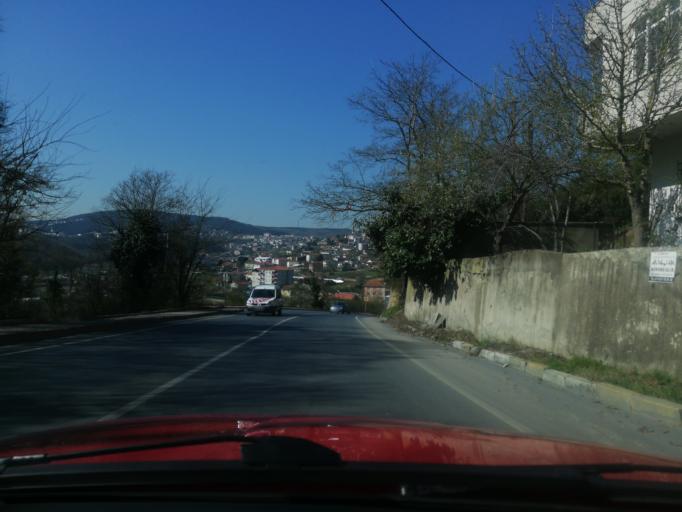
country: TR
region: Istanbul
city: Umraniye
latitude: 41.0761
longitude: 29.1448
